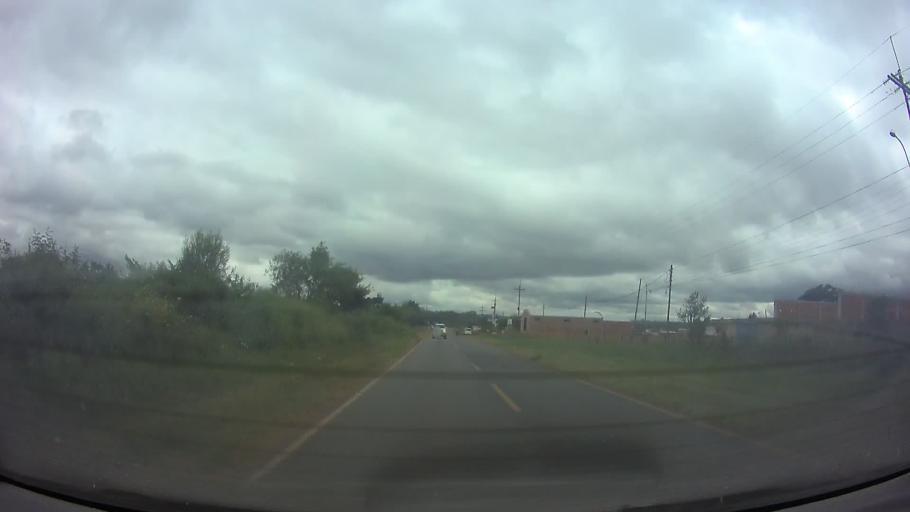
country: PY
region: Central
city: Guarambare
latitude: -25.5004
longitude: -57.4807
